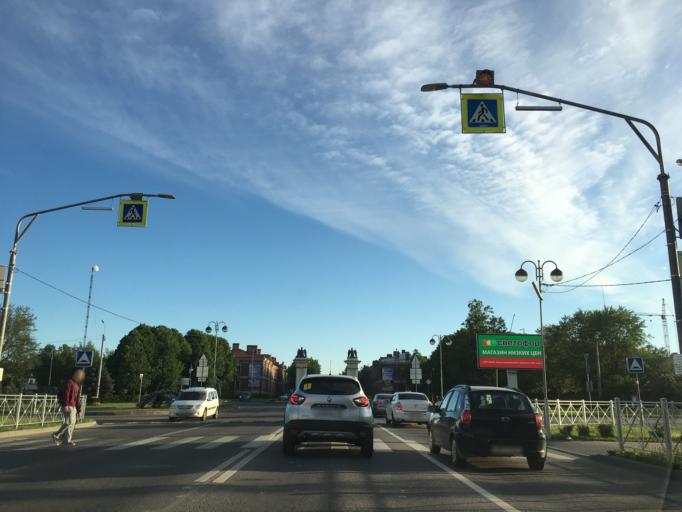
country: RU
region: Leningrad
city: Gatchina
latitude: 59.5773
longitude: 30.1335
